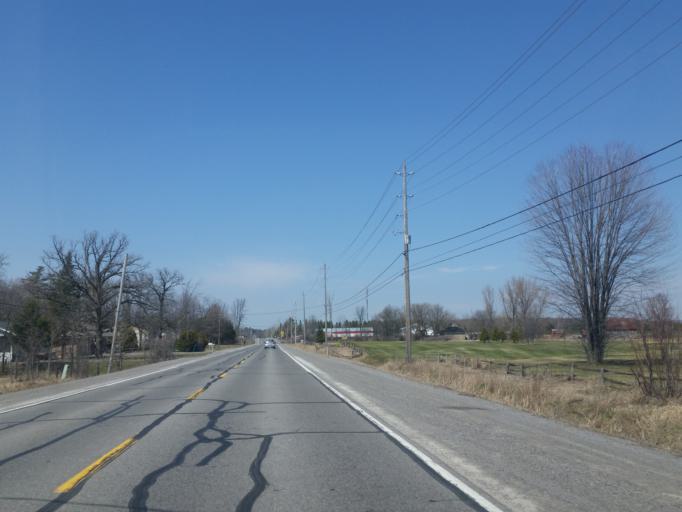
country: CA
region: Ontario
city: Bells Corners
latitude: 45.4564
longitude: -76.0674
